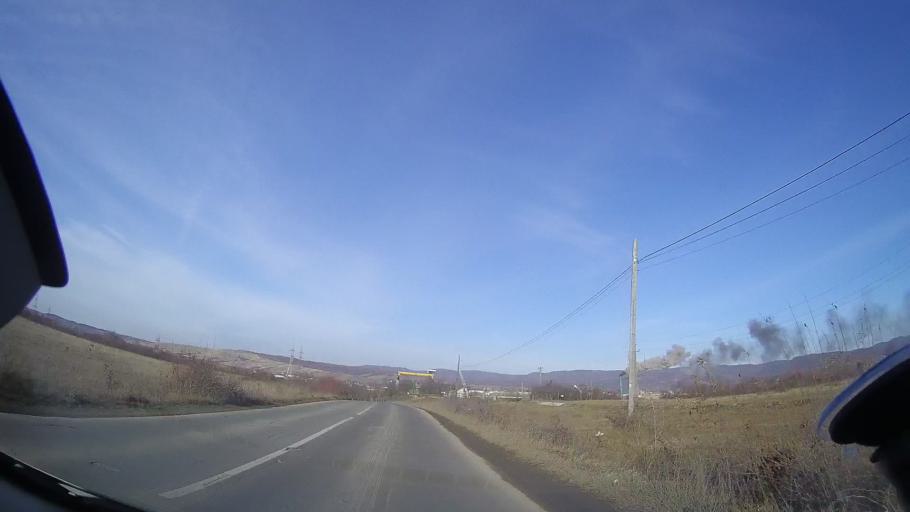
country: RO
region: Bihor
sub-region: Comuna Astileu
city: Astileu
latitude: 47.0403
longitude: 22.3915
